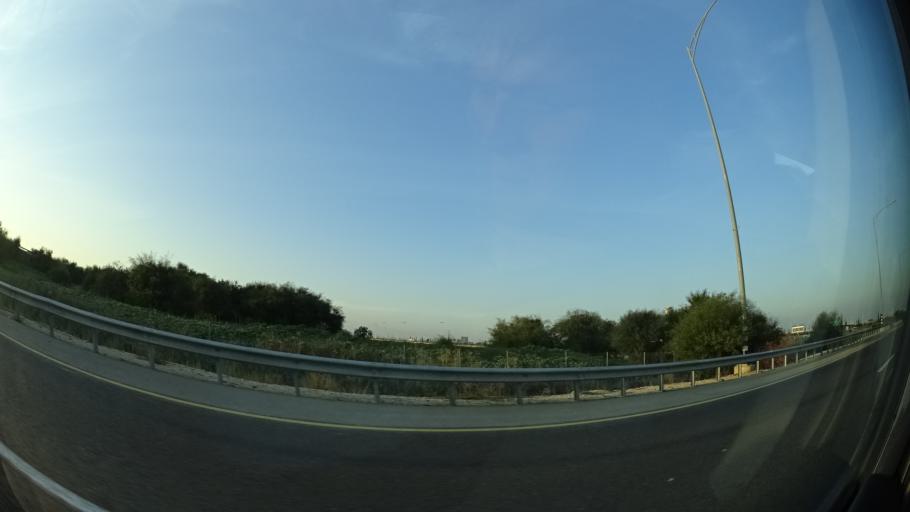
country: IL
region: Central District
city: Kefar Habad
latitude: 31.9936
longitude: 34.8694
